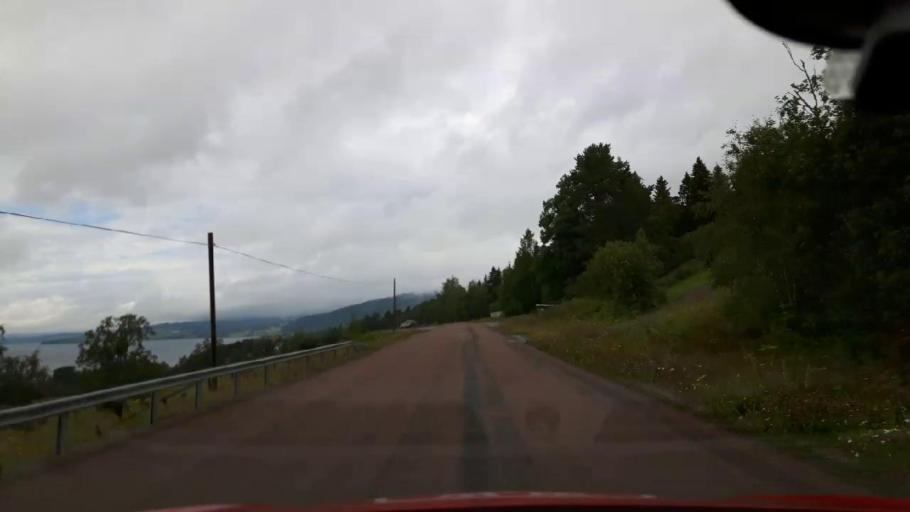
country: SE
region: Jaemtland
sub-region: Krokoms Kommun
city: Valla
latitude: 63.3631
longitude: 14.0631
